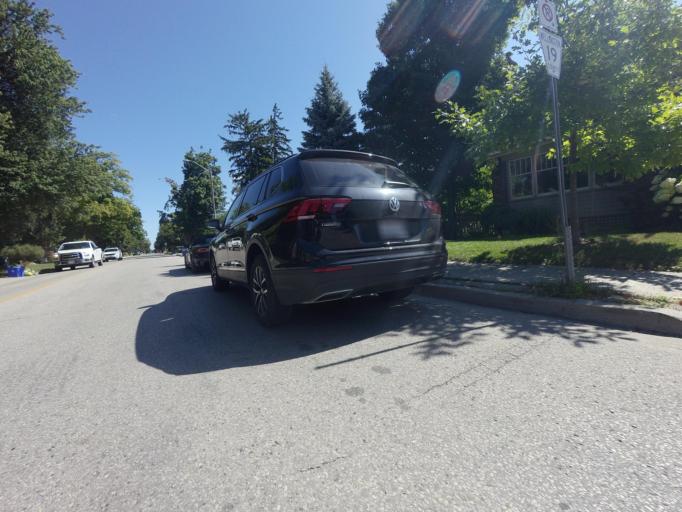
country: CA
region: Ontario
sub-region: Wellington County
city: Guelph
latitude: 43.7080
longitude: -80.3815
